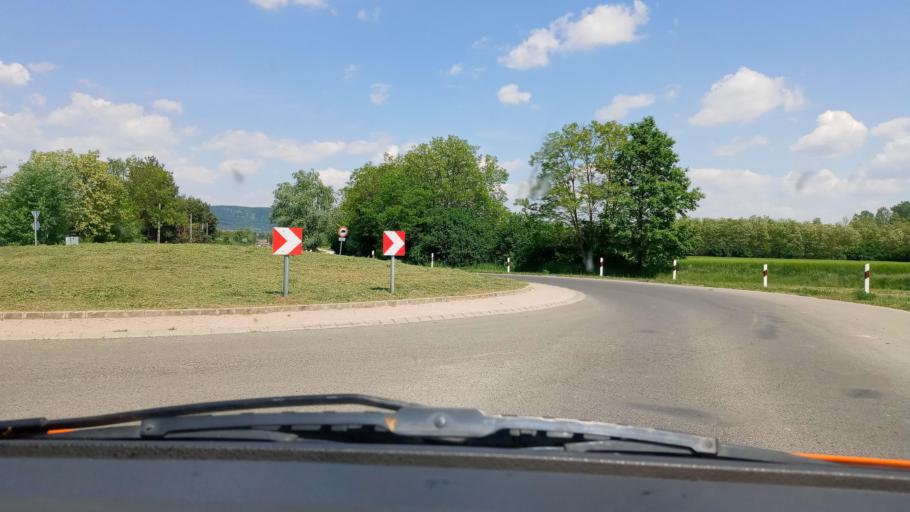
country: HU
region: Baranya
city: Harkany
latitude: 45.8366
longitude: 18.2281
